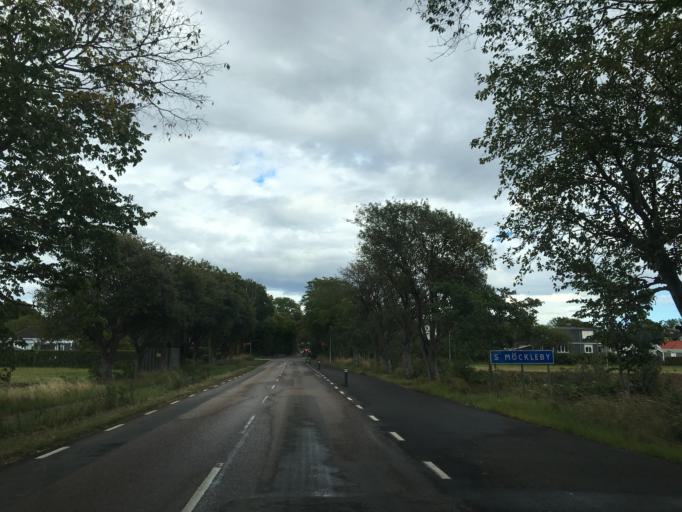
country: SE
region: Kalmar
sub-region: Morbylanga Kommun
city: Moerbylanga
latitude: 56.3560
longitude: 16.4164
